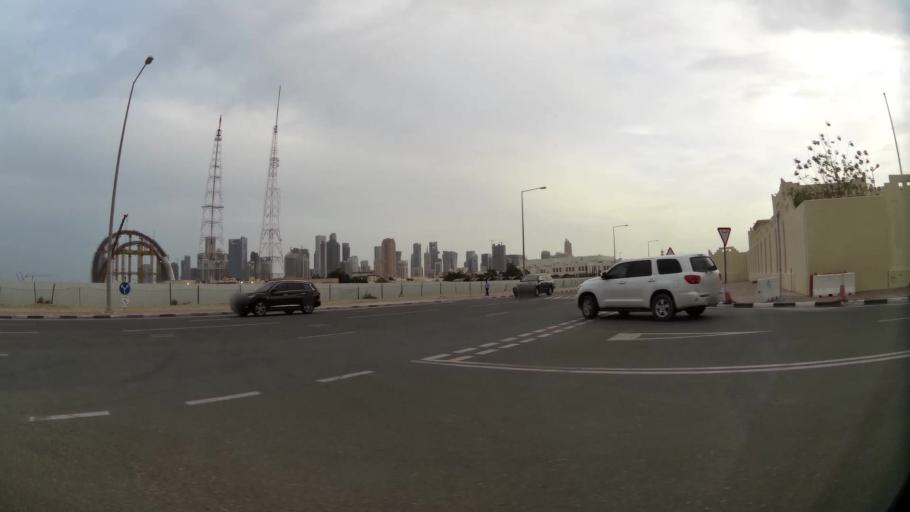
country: QA
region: Baladiyat ad Dawhah
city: Doha
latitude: 25.3369
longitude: 51.5107
